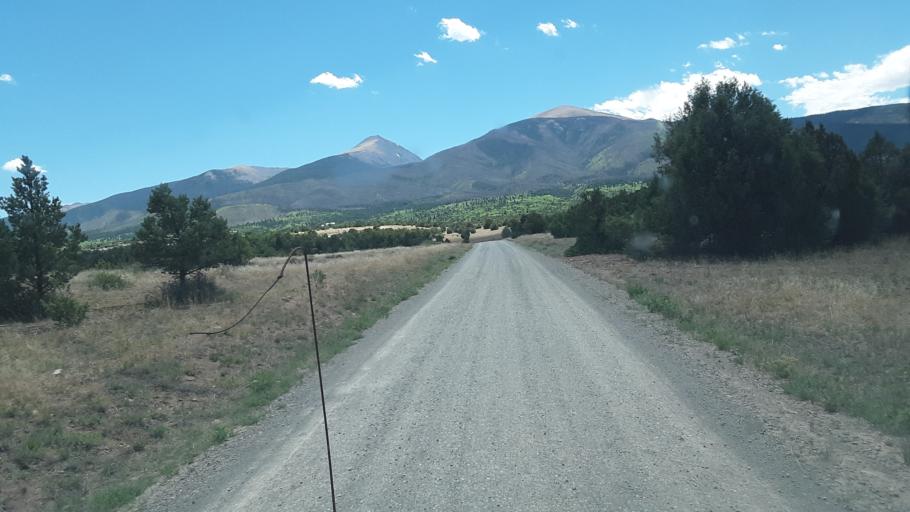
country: US
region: Colorado
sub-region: Custer County
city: Westcliffe
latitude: 38.3102
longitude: -105.6741
